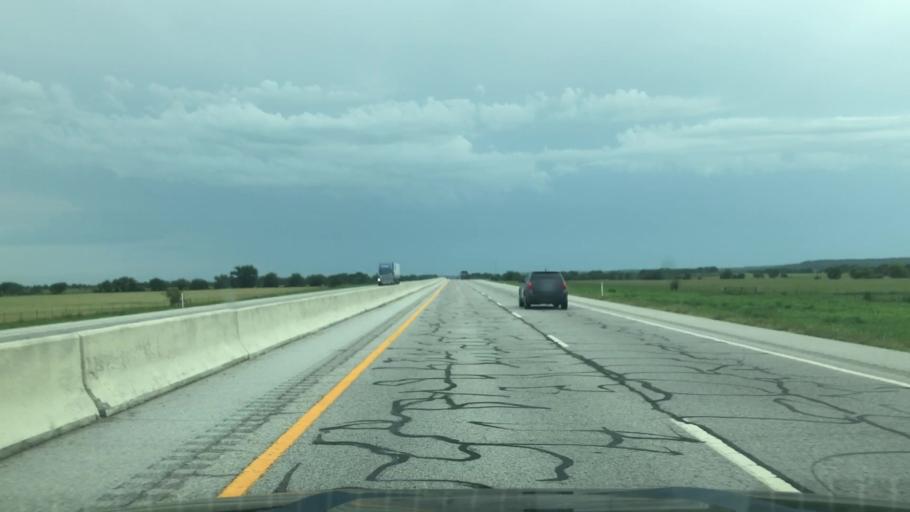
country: US
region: Oklahoma
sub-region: Craig County
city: Vinita
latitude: 36.5377
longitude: -95.2396
